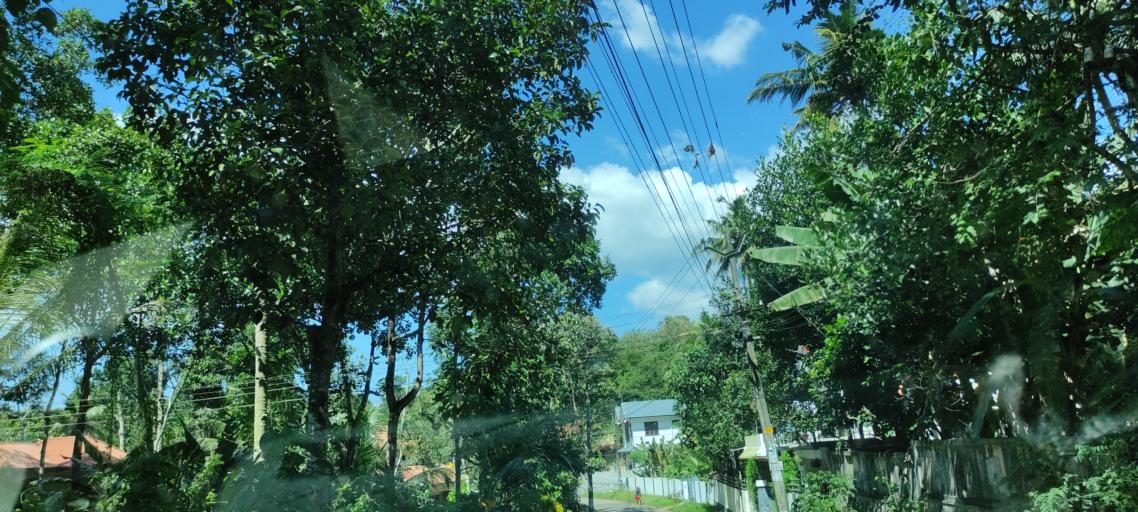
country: IN
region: Kerala
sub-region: Pattanamtitta
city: Adur
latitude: 9.1049
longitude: 76.6884
